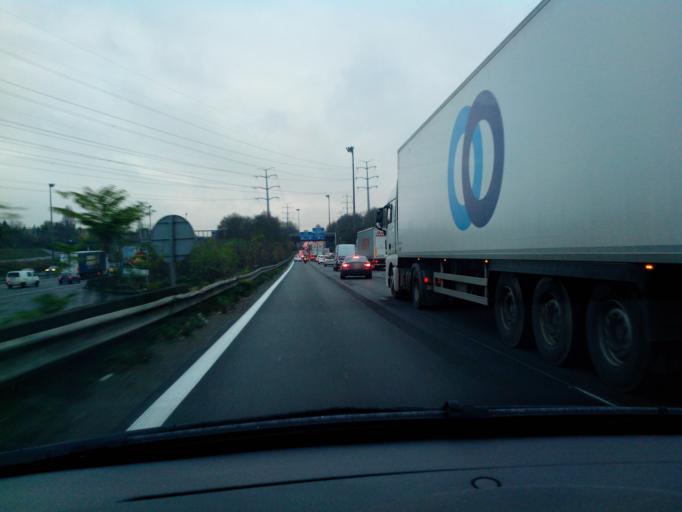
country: FR
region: Ile-de-France
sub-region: Departement du Val-de-Marne
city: Fresnes
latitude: 48.7467
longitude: 2.3250
